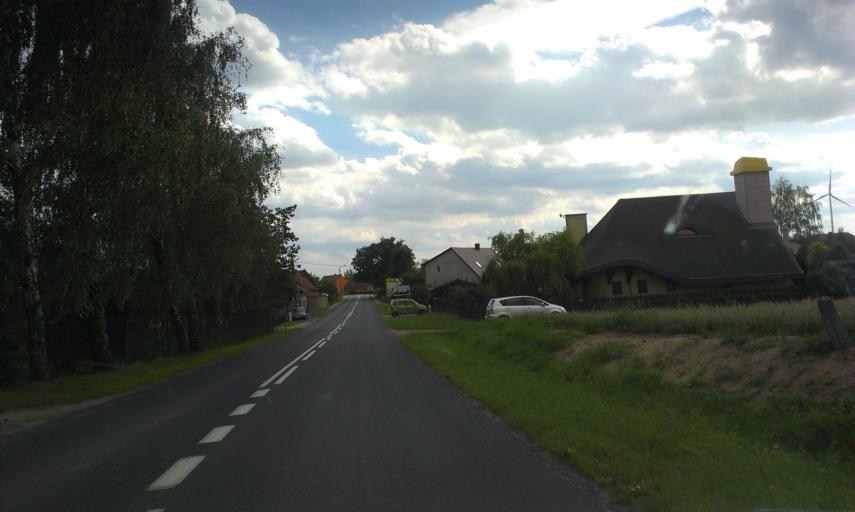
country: PL
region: Greater Poland Voivodeship
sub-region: Powiat zlotowski
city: Zlotow
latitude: 53.3494
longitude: 17.0198
